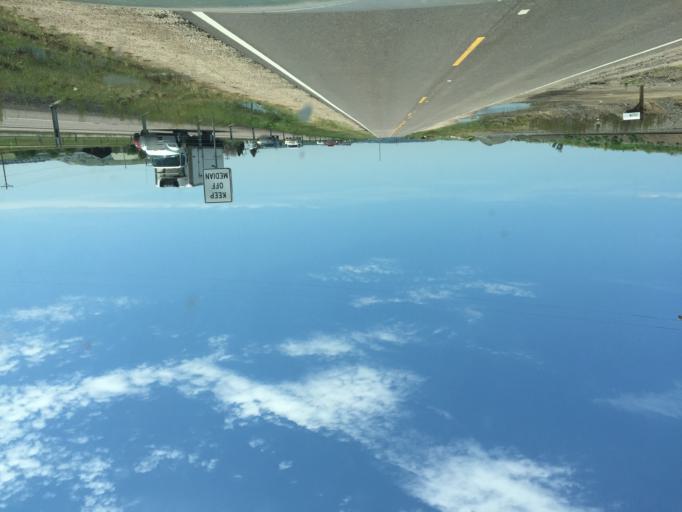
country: US
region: Colorado
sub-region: Douglas County
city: Castle Rock
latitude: 39.3096
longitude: -104.8869
